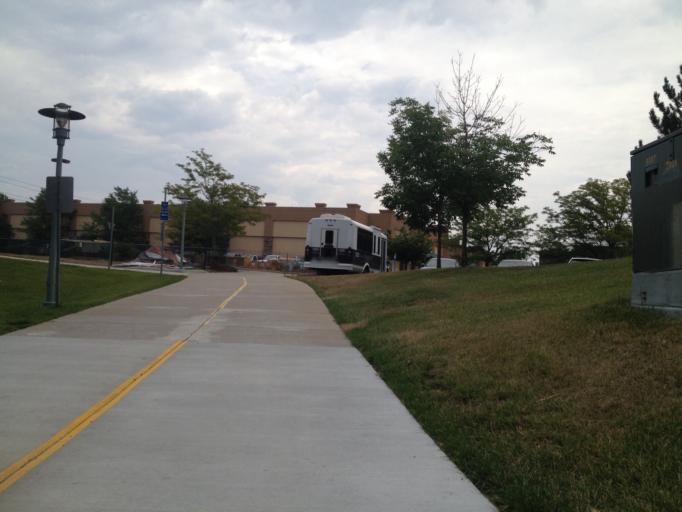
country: US
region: Colorado
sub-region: Broomfield County
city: Broomfield
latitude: 39.9329
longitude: -105.1275
